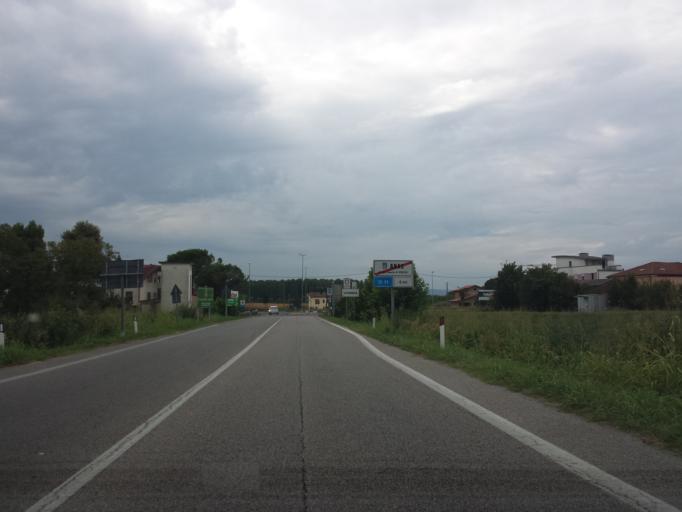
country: IT
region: Veneto
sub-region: Provincia di Vicenza
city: Lisiera
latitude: 45.5761
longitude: 11.5882
